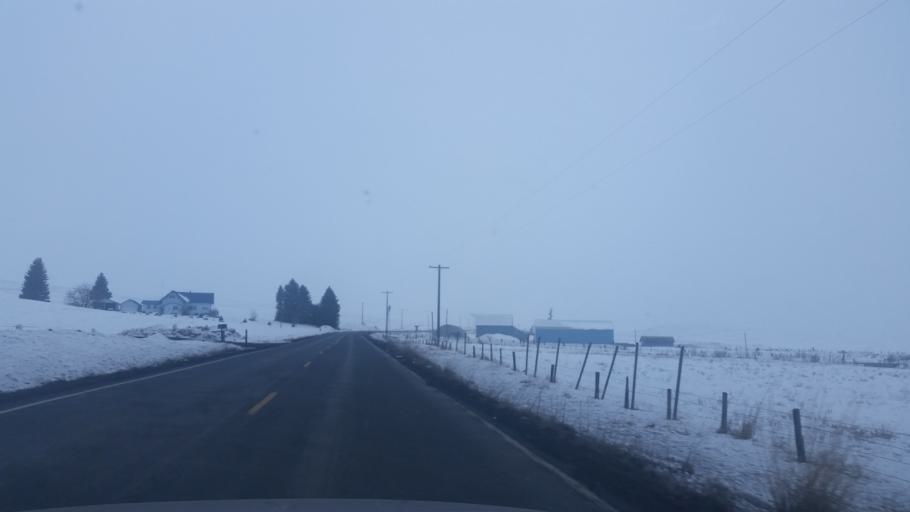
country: US
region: Washington
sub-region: Spokane County
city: Medical Lake
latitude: 47.7157
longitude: -117.8717
